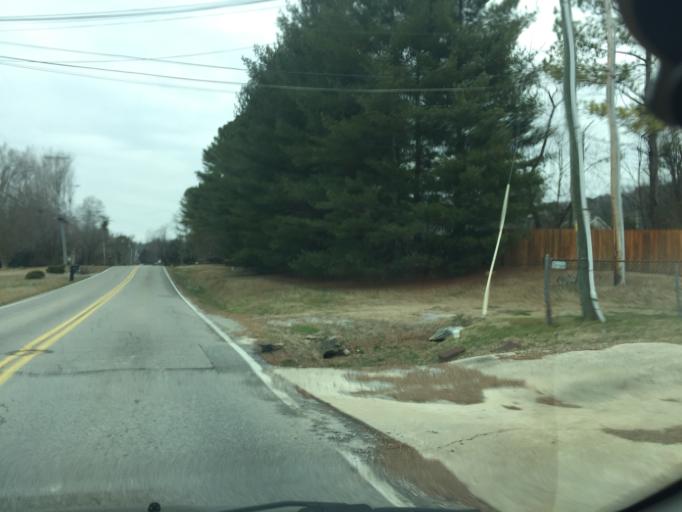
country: US
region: Tennessee
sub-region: Hamilton County
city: East Brainerd
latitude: 35.0066
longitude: -85.1297
